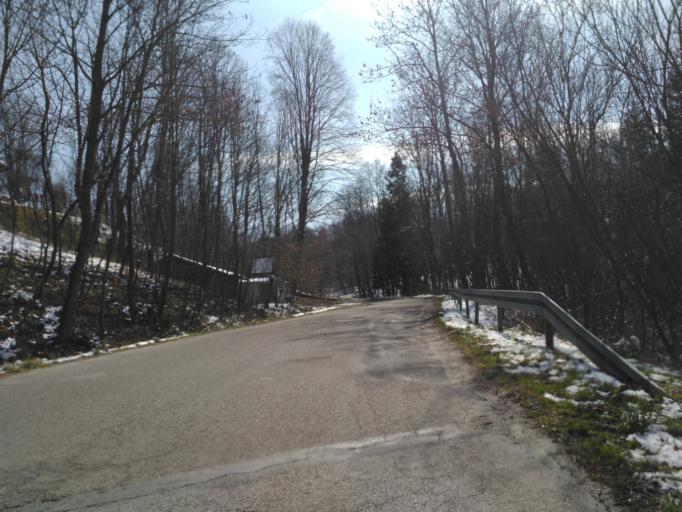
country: PL
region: Subcarpathian Voivodeship
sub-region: Powiat ropczycko-sedziszowski
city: Wielopole Skrzynskie
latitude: 49.9869
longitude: 21.5894
